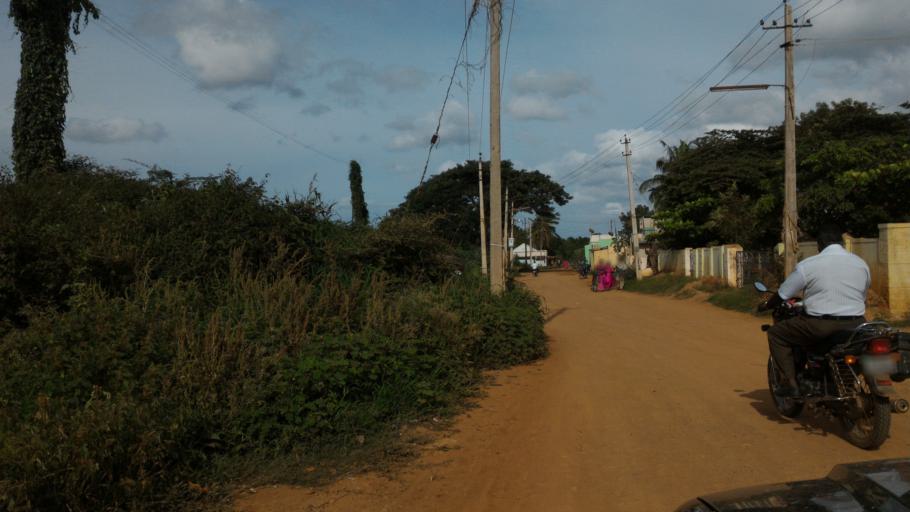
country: IN
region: Karnataka
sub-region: Tumkur
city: Gubbi
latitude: 13.3217
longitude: 76.9412
